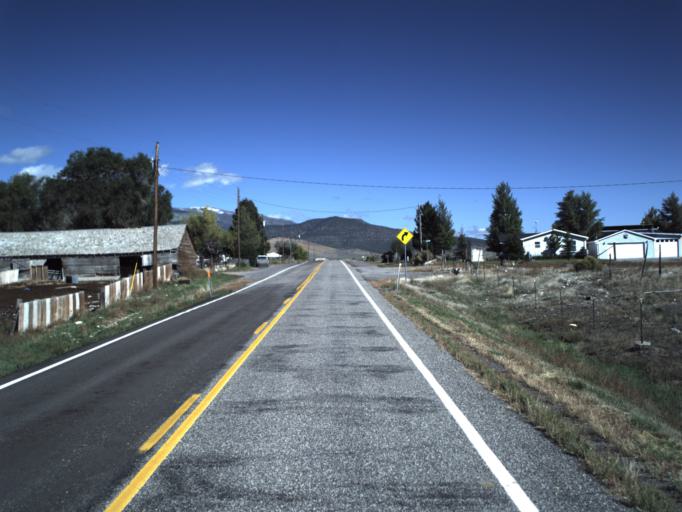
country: US
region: Utah
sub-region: Wayne County
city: Loa
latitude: 38.4298
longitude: -111.9226
